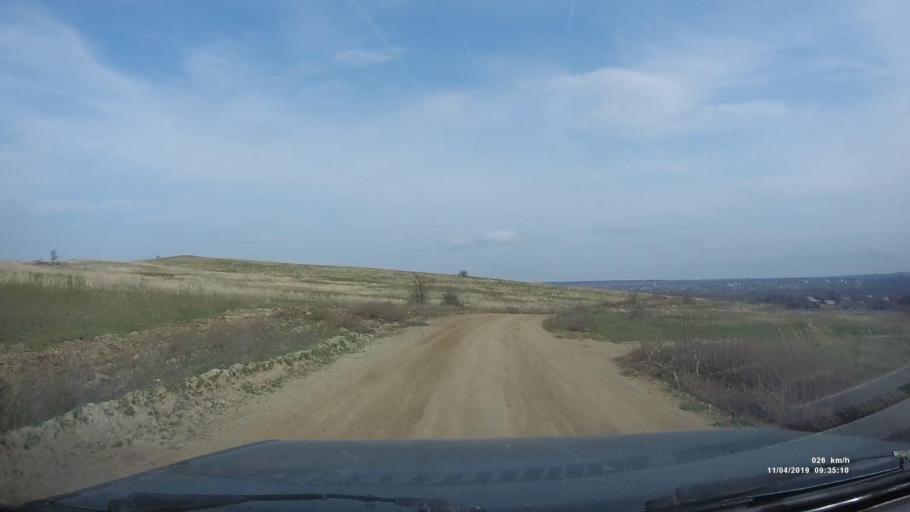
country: RU
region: Rostov
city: Staraya Stanitsa
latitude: 48.2714
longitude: 40.3715
